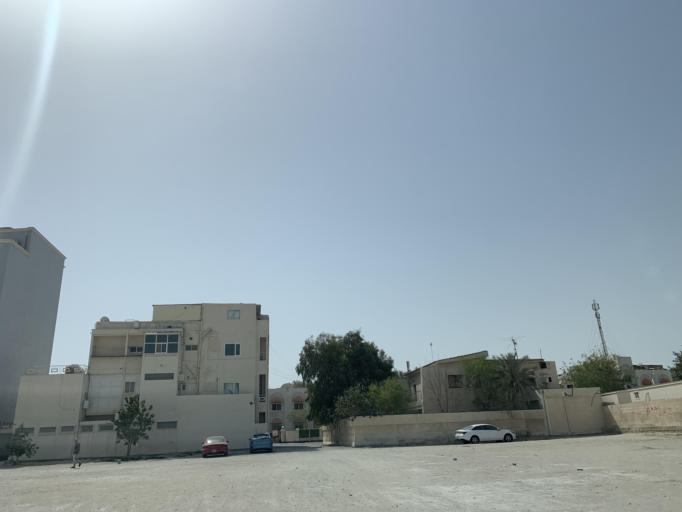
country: BH
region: Manama
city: Manama
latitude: 26.2087
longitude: 50.5885
